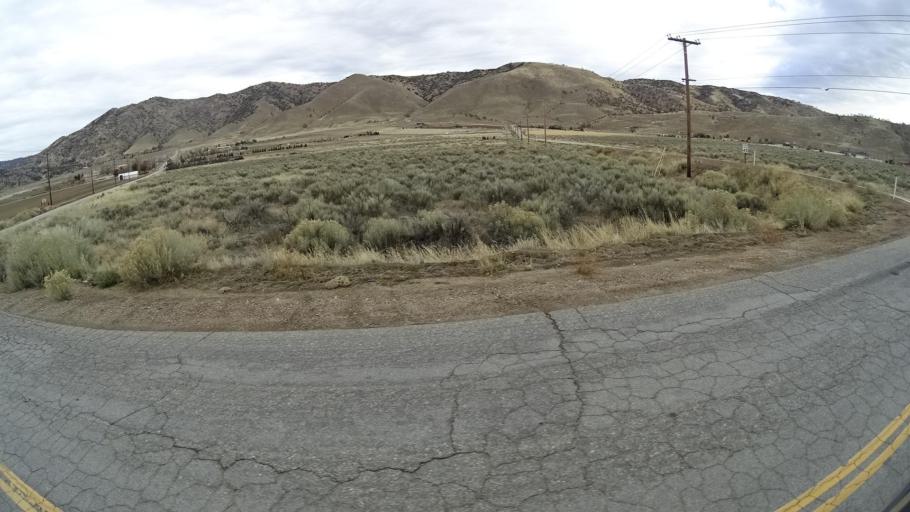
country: US
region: California
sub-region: Kern County
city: Bear Valley Springs
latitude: 35.1242
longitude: -118.5742
